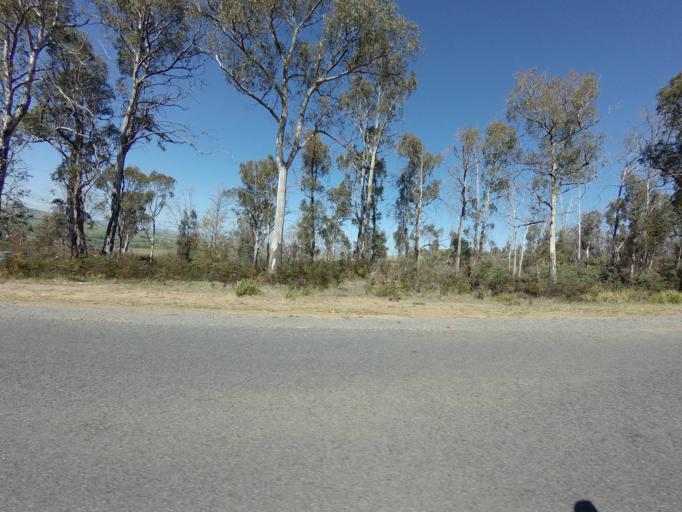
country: AU
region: Tasmania
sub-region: Derwent Valley
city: New Norfolk
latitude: -42.5414
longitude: 146.7201
